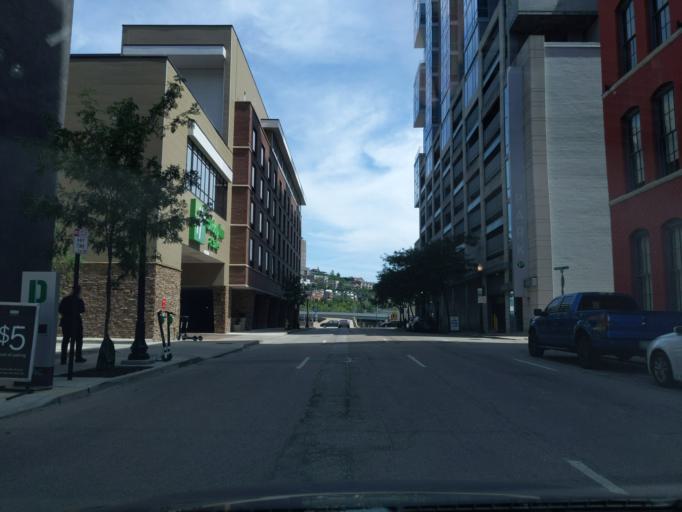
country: US
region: Kentucky
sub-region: Campbell County
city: Newport
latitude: 39.1045
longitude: -84.5082
